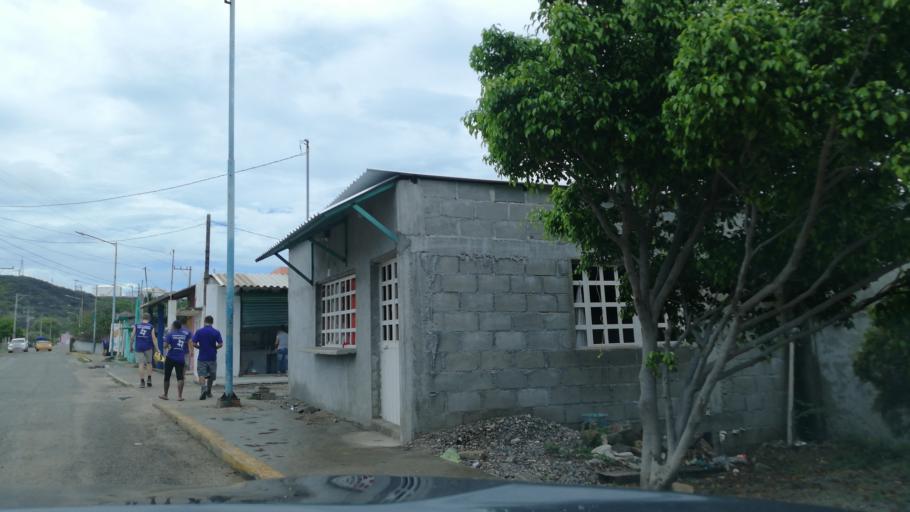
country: MX
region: Oaxaca
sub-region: Salina Cruz
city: Salina Cruz
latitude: 16.1632
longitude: -95.2208
